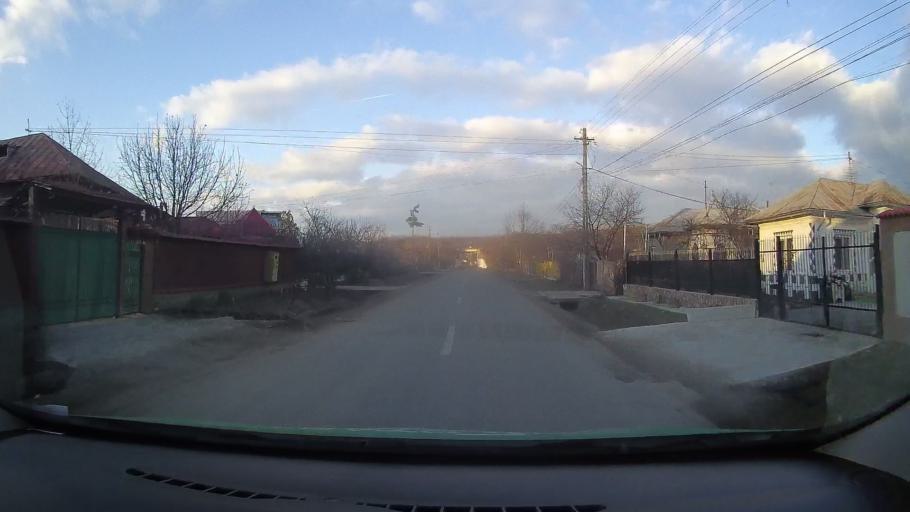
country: RO
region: Dambovita
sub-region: Comuna Gura Ocnitei
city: Adanca
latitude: 44.9145
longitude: 25.6152
